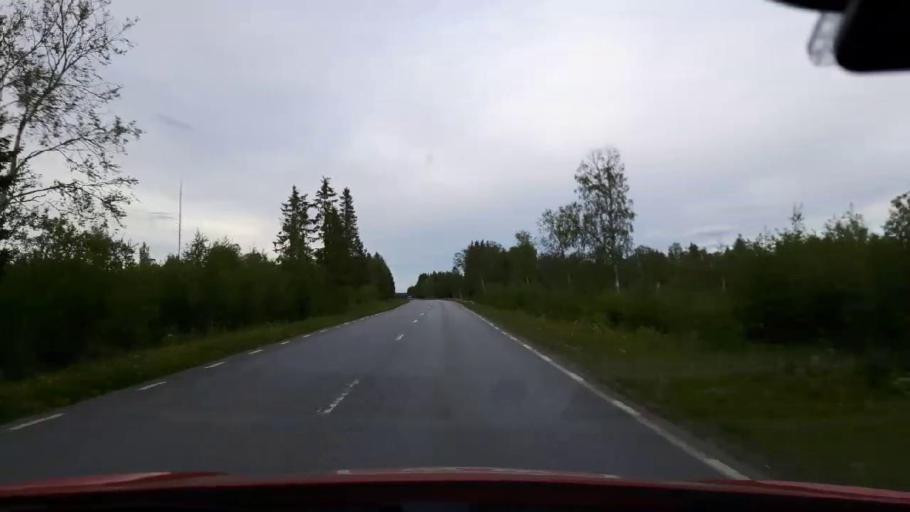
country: SE
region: Jaemtland
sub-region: Bergs Kommun
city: Hoverberg
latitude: 62.9657
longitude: 14.5227
